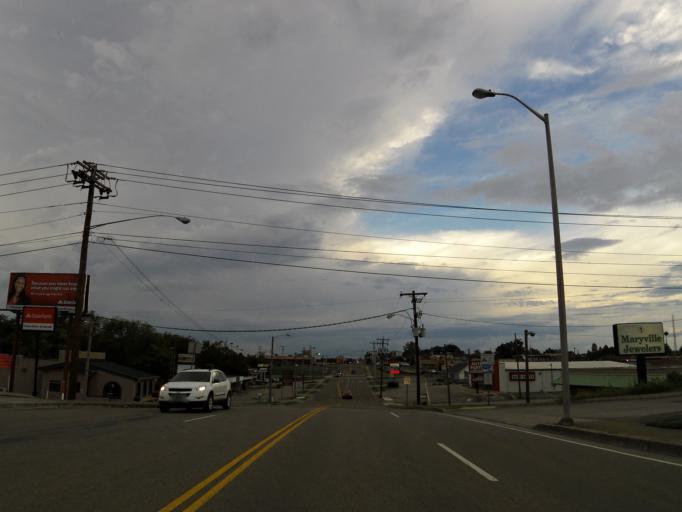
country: US
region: Tennessee
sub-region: Blount County
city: Maryville
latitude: 35.7581
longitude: -83.9743
